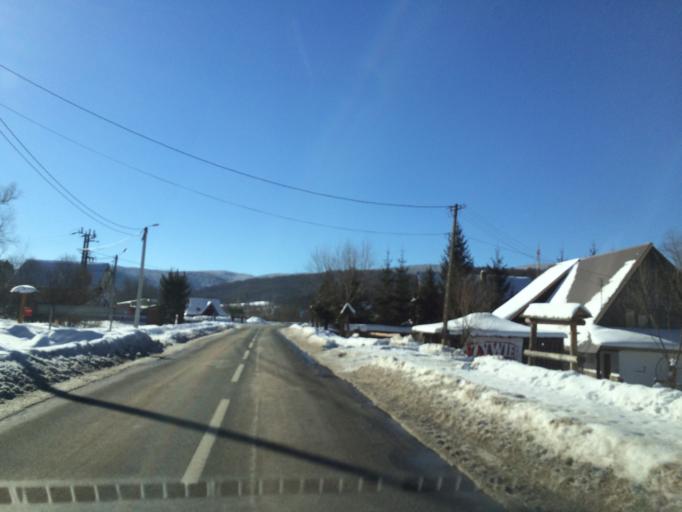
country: PL
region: Subcarpathian Voivodeship
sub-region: Powiat bieszczadzki
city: Lutowiska
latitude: 49.1065
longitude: 22.6500
